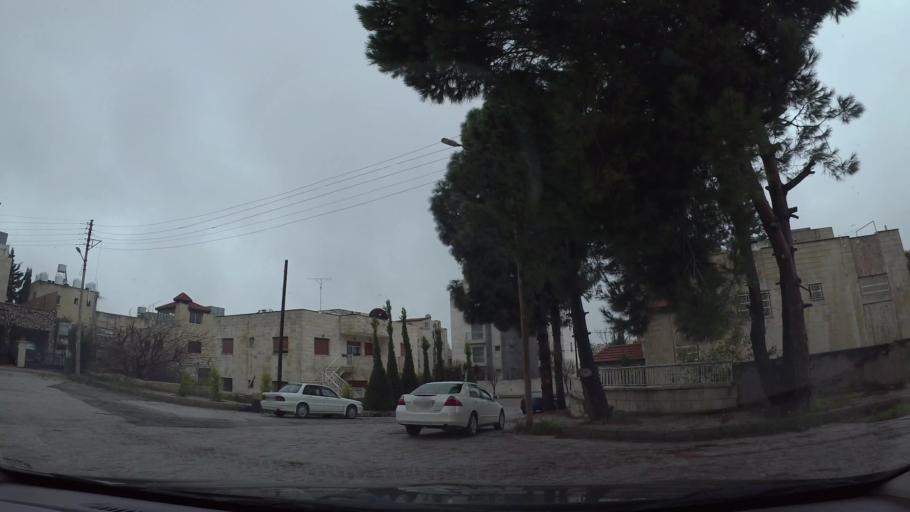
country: JO
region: Amman
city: Wadi as Sir
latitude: 31.9690
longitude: 35.8457
